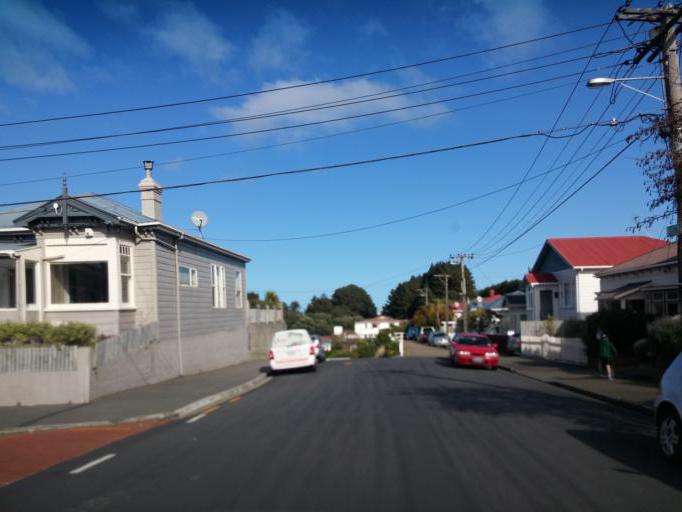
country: NZ
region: Wellington
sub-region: Wellington City
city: Brooklyn
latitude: -41.3220
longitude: 174.7726
